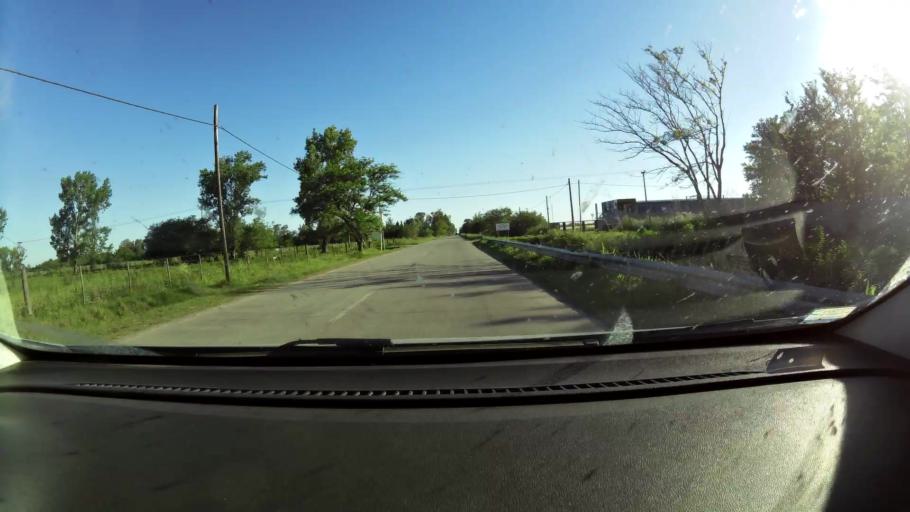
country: AR
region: Cordoba
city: San Francisco
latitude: -31.4467
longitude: -62.1011
